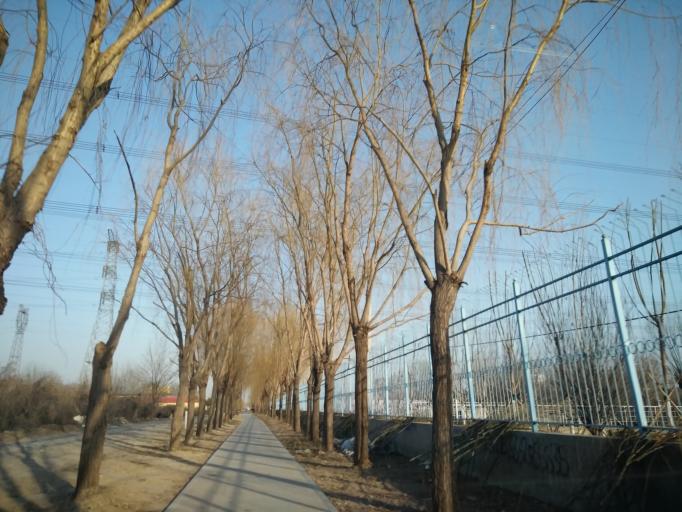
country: CN
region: Beijing
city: Xingfeng
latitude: 39.7213
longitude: 116.3812
